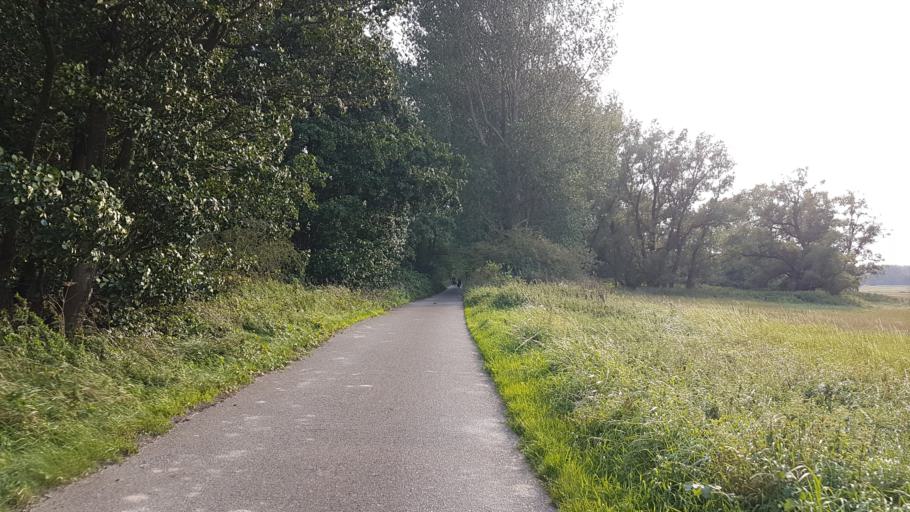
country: DE
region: Mecklenburg-Vorpommern
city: Sagard
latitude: 54.5109
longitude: 13.5271
